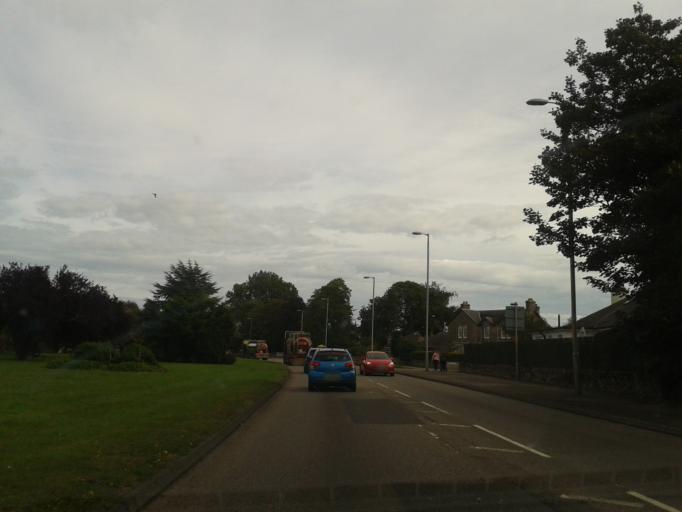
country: GB
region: Scotland
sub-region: Highland
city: Nairn
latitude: 57.5799
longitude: -3.8827
